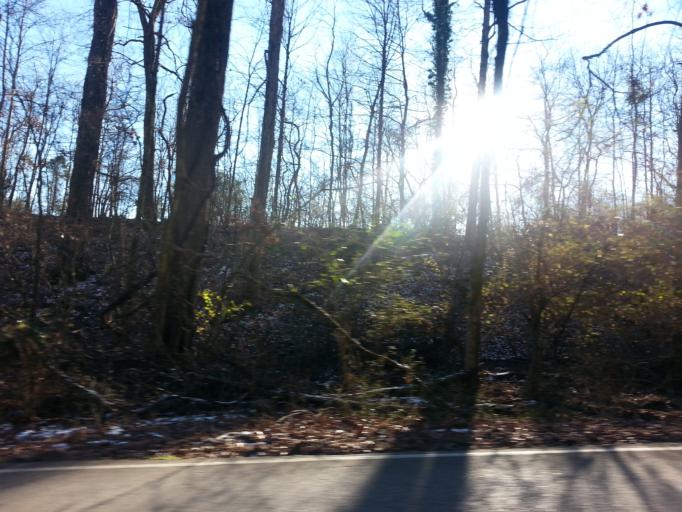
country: US
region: Tennessee
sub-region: Knox County
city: Knoxville
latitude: 35.8974
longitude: -83.9775
